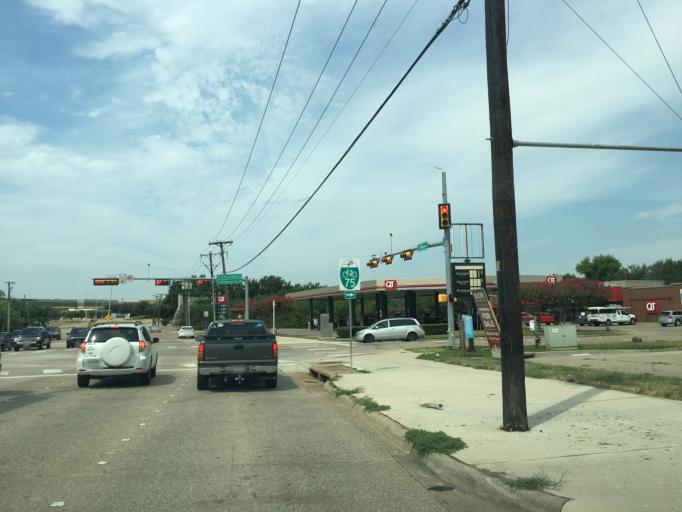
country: US
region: Texas
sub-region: Collin County
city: Plano
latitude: 33.0282
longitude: -96.7123
